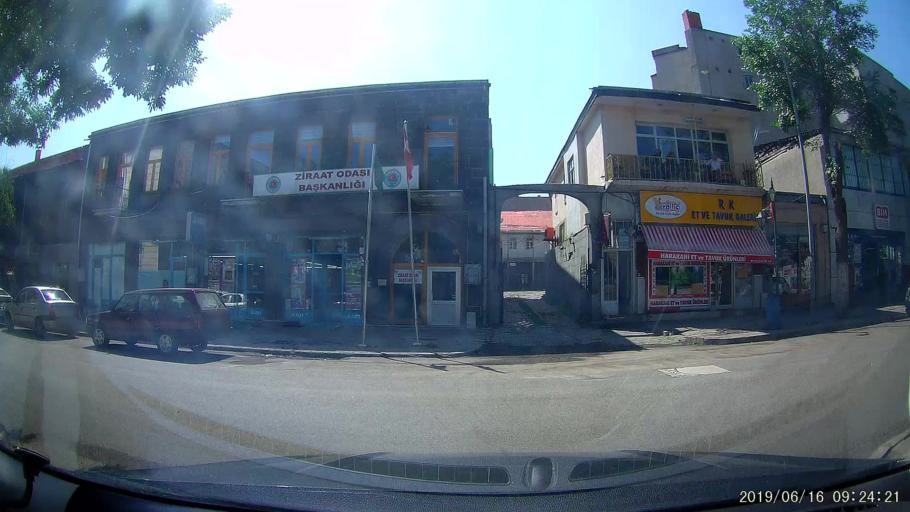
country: TR
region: Kars
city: Kars
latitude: 40.6089
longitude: 43.0935
